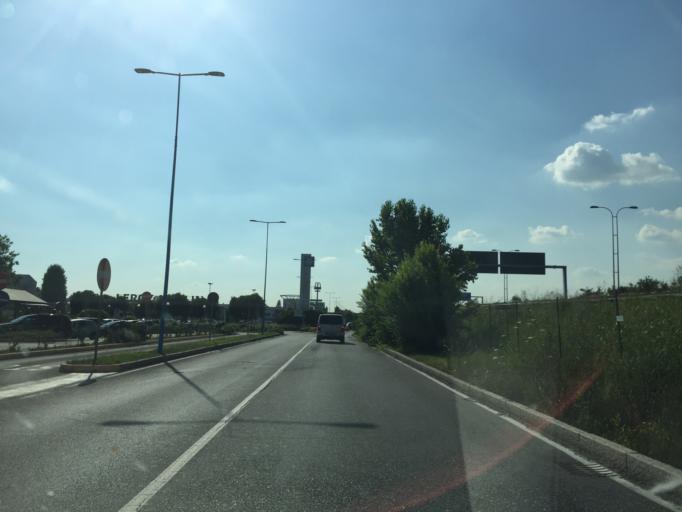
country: IT
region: Lombardy
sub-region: Provincia di Brescia
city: Brescia
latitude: 45.5215
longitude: 10.1871
